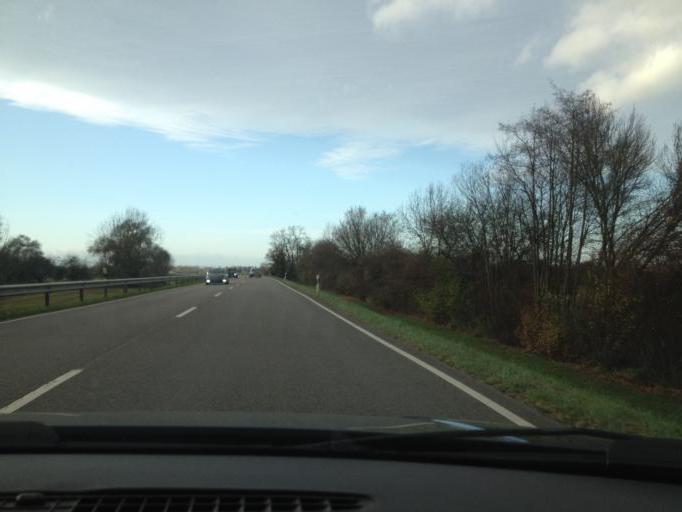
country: DE
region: Baden-Wuerttemberg
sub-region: Karlsruhe Region
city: Altlussheim
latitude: 49.3107
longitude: 8.4817
